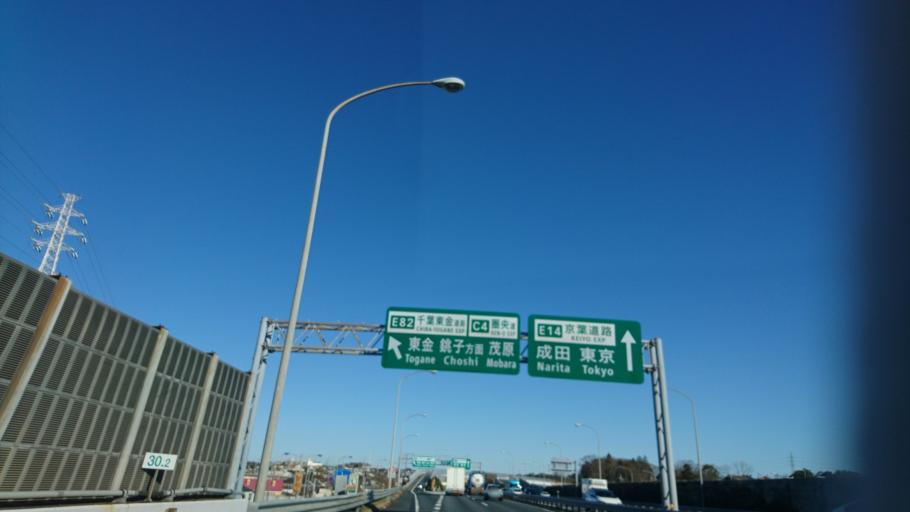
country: JP
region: Chiba
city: Chiba
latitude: 35.5999
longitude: 140.1494
